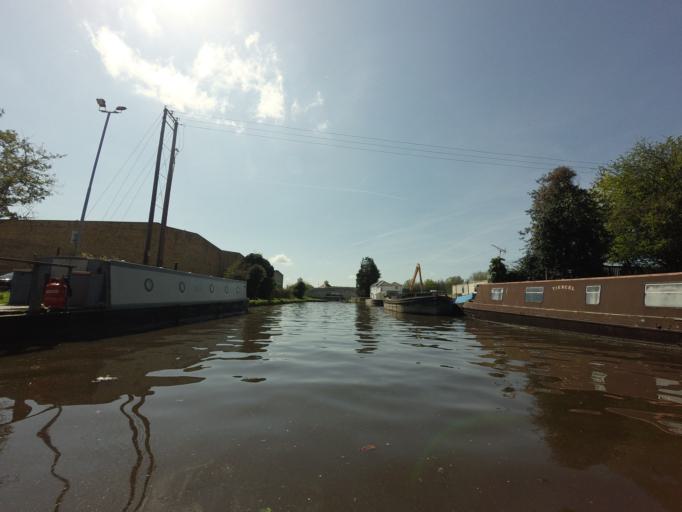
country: GB
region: England
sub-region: Greater London
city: Hayes
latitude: 51.5008
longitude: -0.4058
